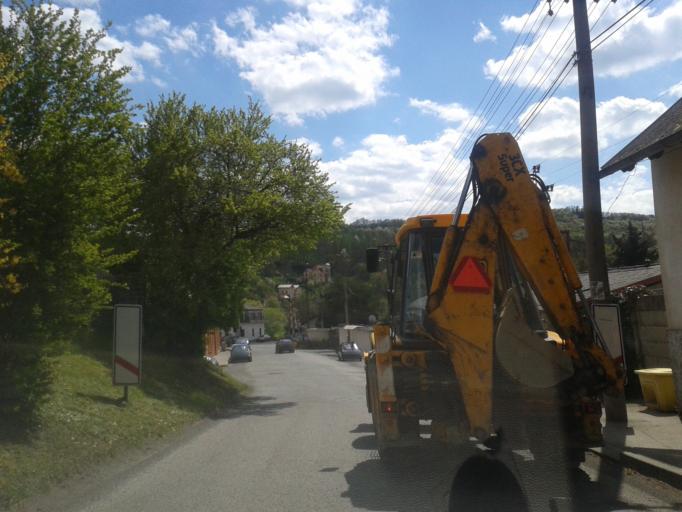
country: CZ
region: Central Bohemia
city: Nizbor
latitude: 50.0035
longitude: 14.0025
